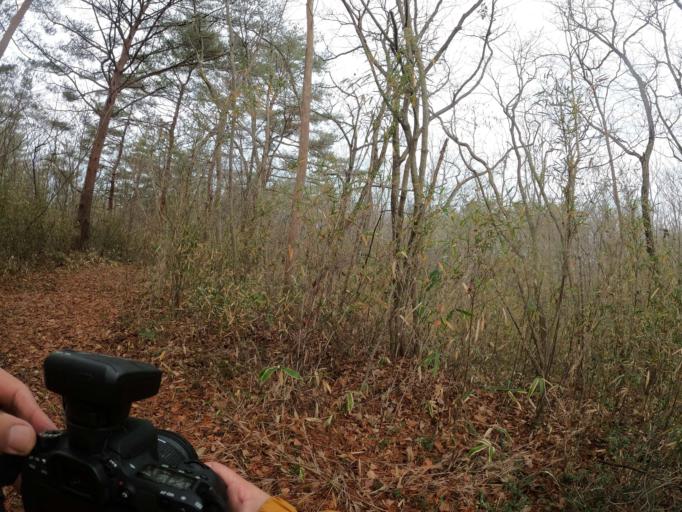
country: JP
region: Iwate
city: Ichinoseki
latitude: 38.8784
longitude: 141.1327
